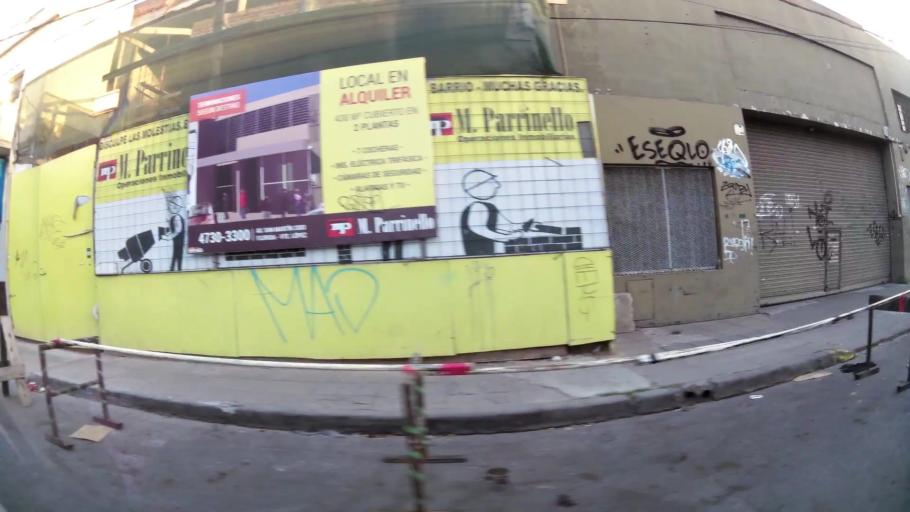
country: AR
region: Buenos Aires
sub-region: Partido de Vicente Lopez
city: Olivos
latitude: -34.5348
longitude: -58.5060
